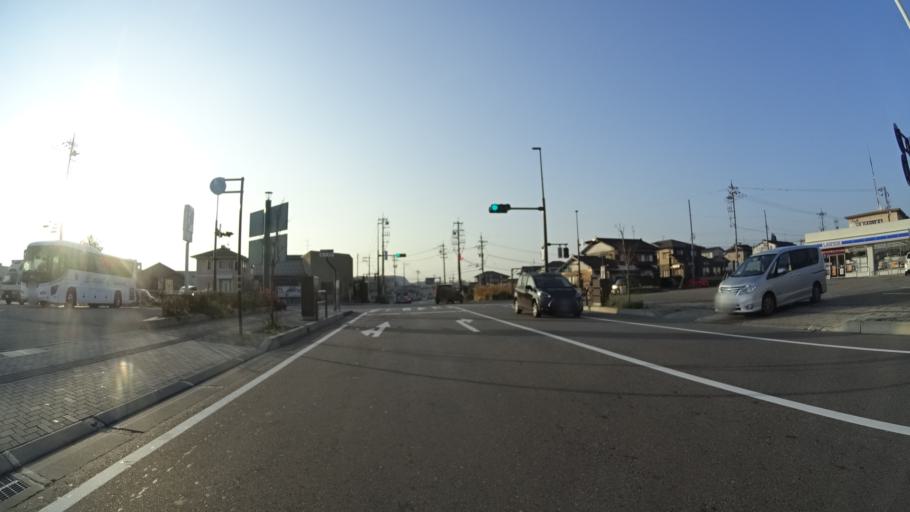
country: JP
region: Ishikawa
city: Nanao
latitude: 37.0839
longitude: 136.9256
